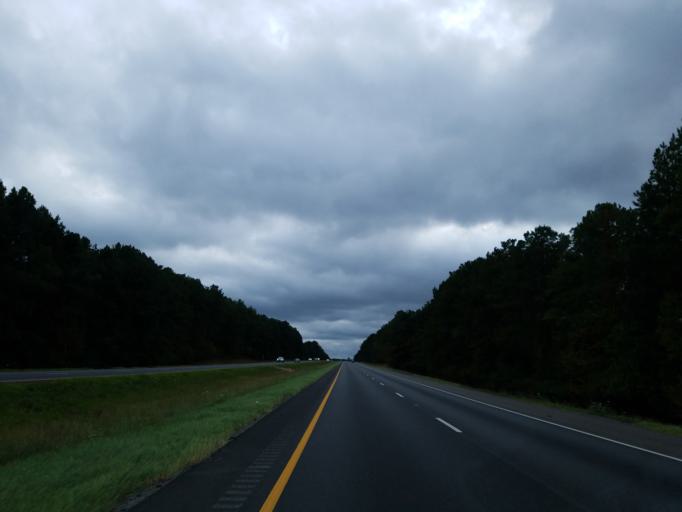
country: US
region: Alabama
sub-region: Hale County
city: Moundville
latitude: 33.0270
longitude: -87.7440
